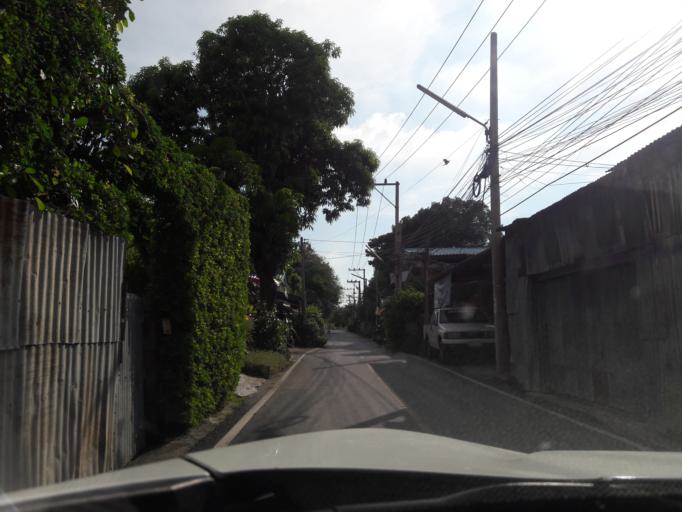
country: TH
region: Lop Buri
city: Ban Mi
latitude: 15.0459
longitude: 100.5376
